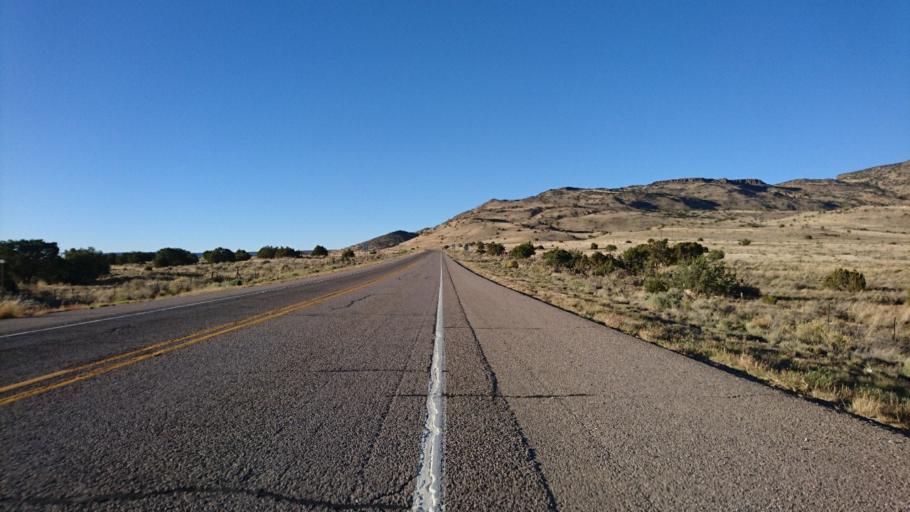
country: US
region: New Mexico
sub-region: Cibola County
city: Grants
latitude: 35.1084
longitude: -107.7809
